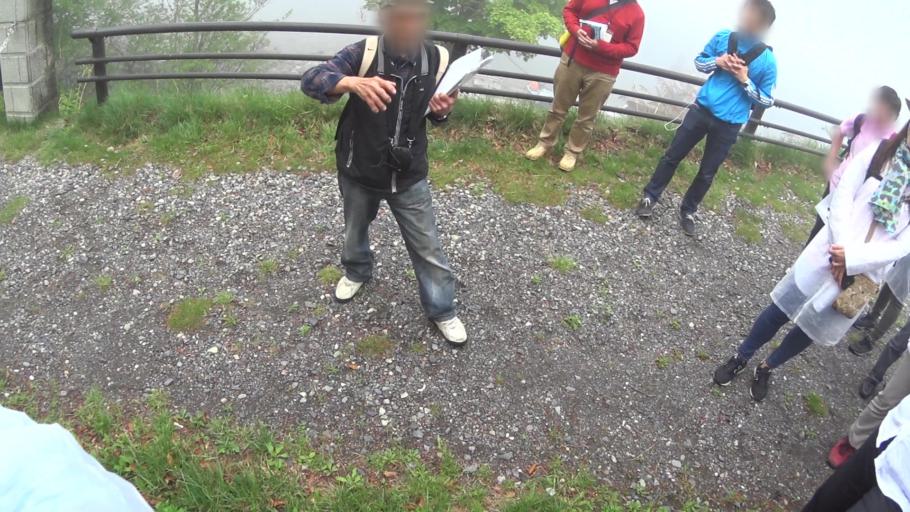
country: JP
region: Tochigi
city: Nikko
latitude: 36.7344
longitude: 139.4931
